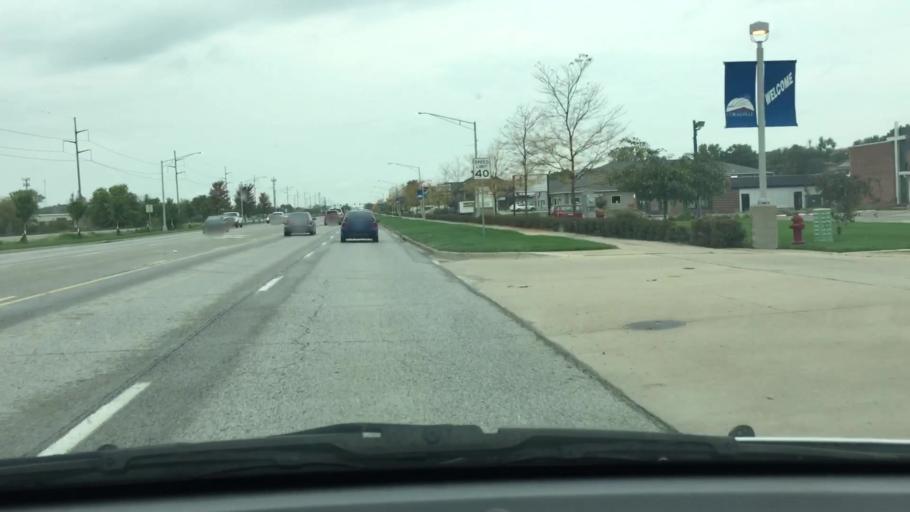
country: US
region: Iowa
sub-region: Johnson County
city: Coralville
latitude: 41.6765
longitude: -91.5855
